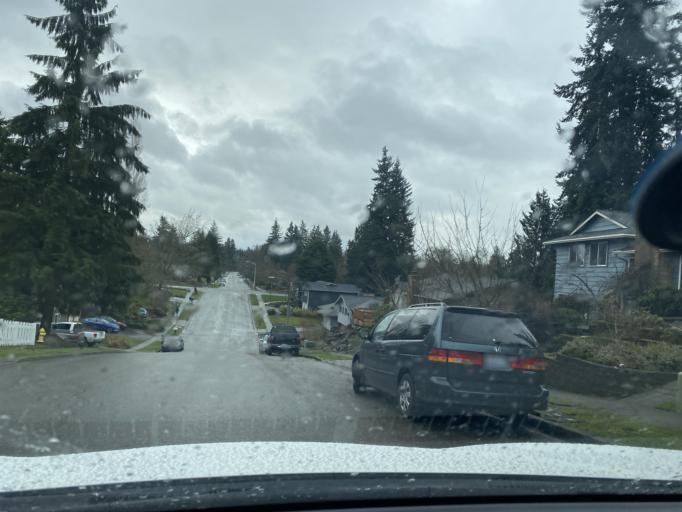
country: US
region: Washington
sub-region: Snohomish County
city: Lynnwood
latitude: 47.8415
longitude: -122.3108
